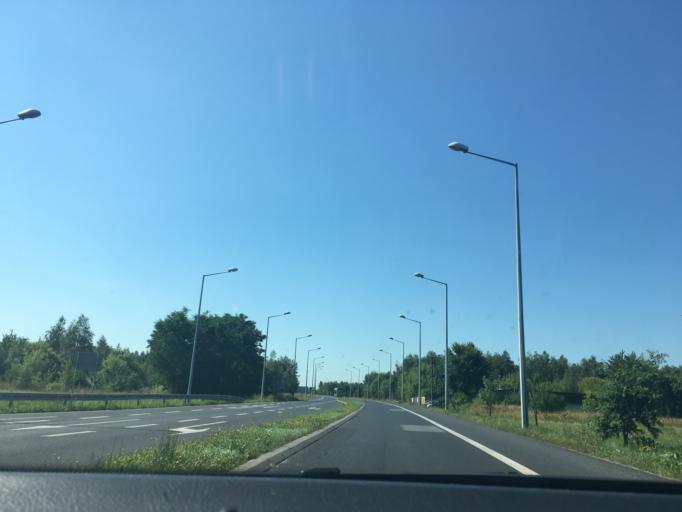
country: PL
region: Lublin Voivodeship
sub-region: Powiat lubartowski
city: Lubartow
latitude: 51.4623
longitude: 22.5765
